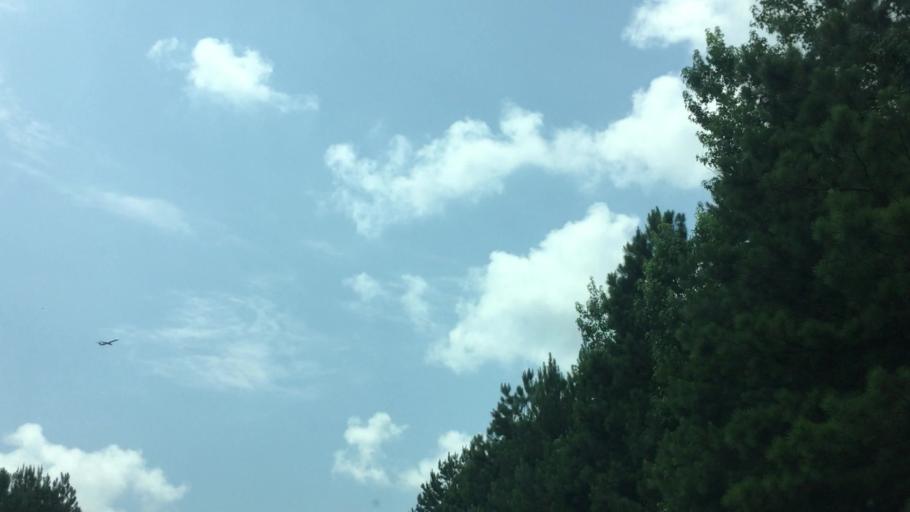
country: US
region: Georgia
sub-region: Fulton County
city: Chattahoochee Hills
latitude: 33.5654
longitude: -84.7403
